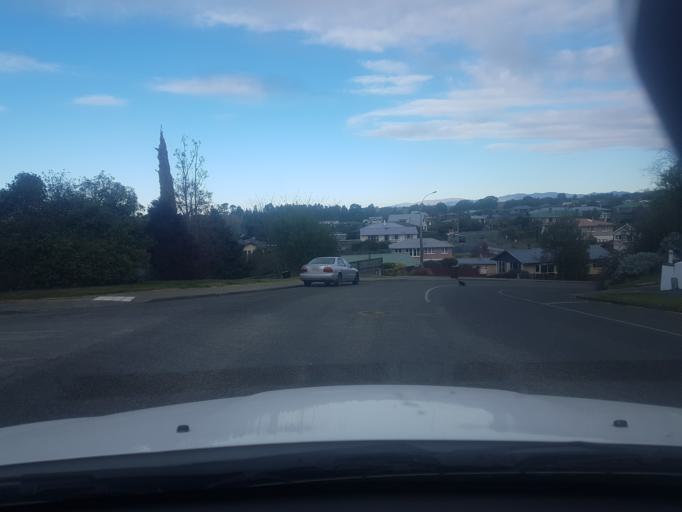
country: NZ
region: Canterbury
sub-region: Timaru District
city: Timaru
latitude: -44.3923
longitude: 171.2196
